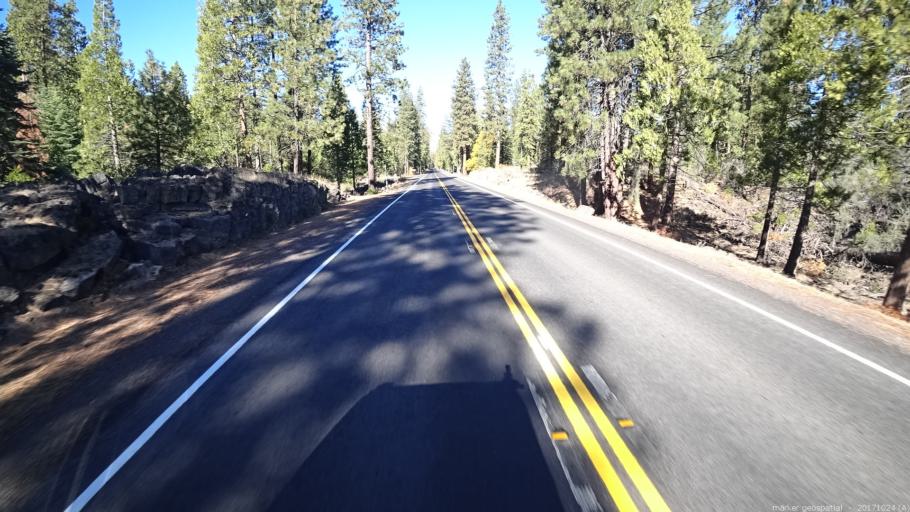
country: US
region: California
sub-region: Shasta County
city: Burney
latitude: 40.7529
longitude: -121.4902
